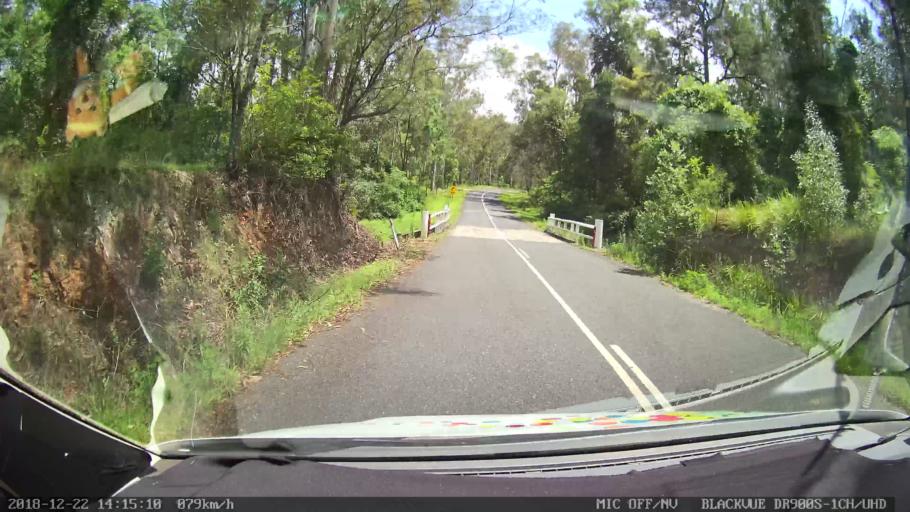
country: AU
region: New South Wales
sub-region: Clarence Valley
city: Coutts Crossing
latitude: -30.0003
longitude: 152.6806
